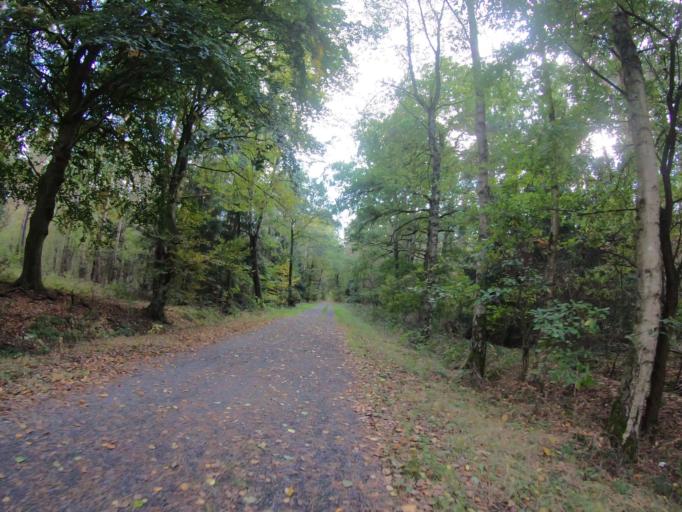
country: DE
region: Lower Saxony
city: Isenbuttel
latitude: 52.4508
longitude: 10.5735
